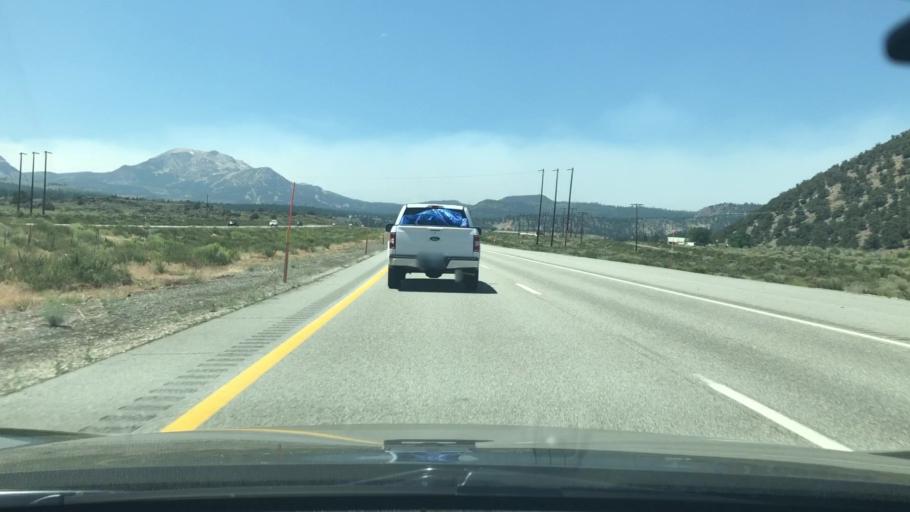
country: US
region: California
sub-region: Mono County
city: Mammoth Lakes
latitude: 37.6363
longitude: -118.8892
